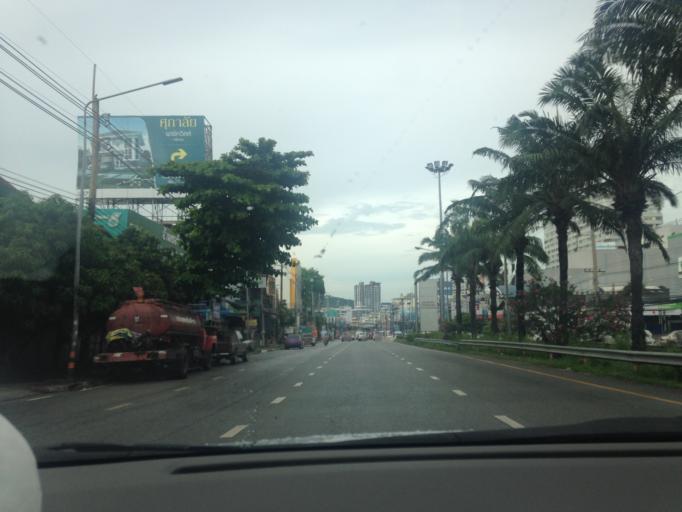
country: TH
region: Chon Buri
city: Si Racha
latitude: 13.1616
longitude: 100.9263
